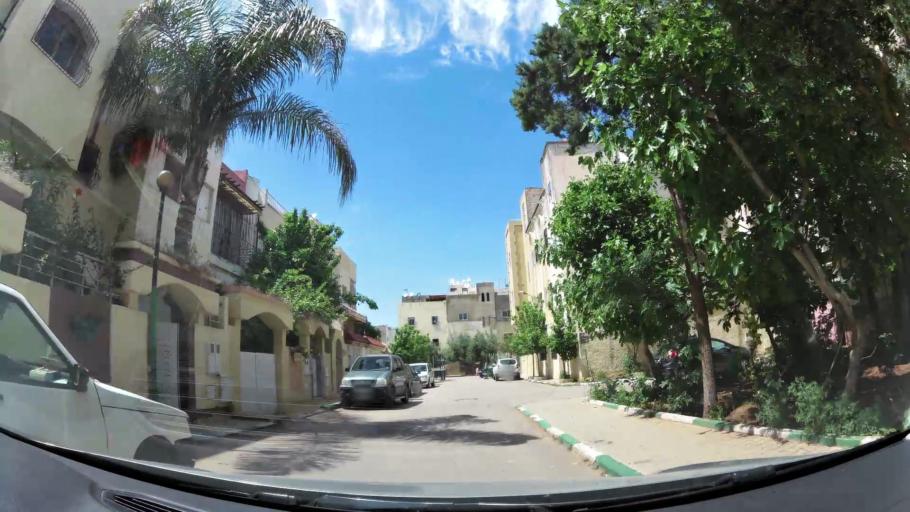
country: MA
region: Fes-Boulemane
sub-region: Fes
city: Fes
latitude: 34.0093
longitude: -4.9892
